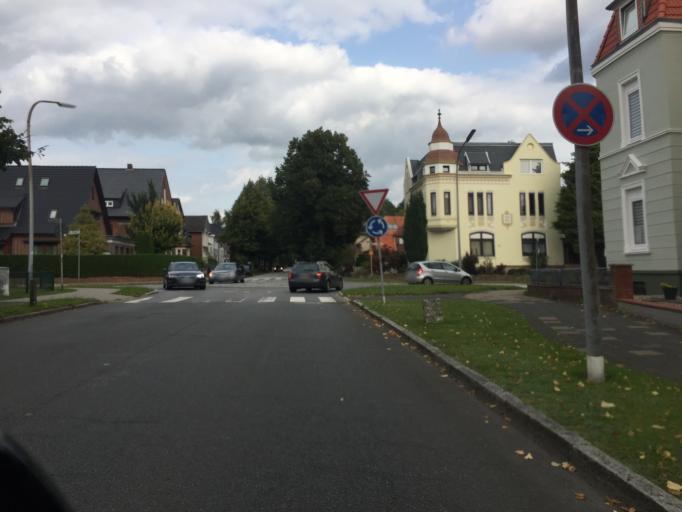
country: DE
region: Schleswig-Holstein
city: Itzehoe
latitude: 53.9327
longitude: 9.5060
